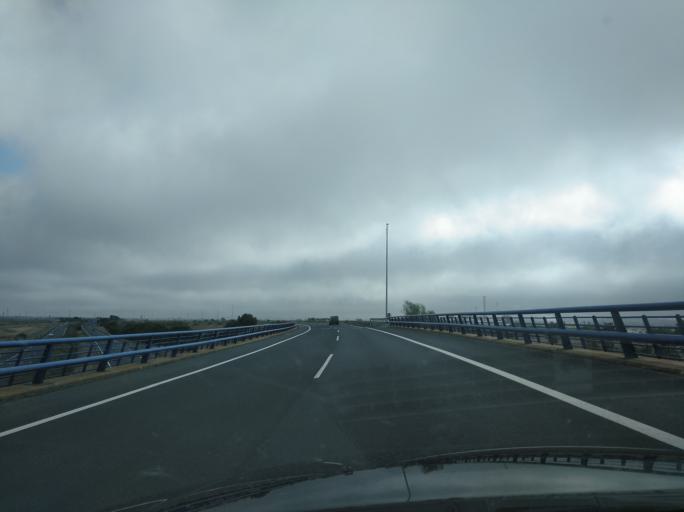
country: ES
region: Andalusia
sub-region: Provincia de Huelva
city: San Juan del Puerto
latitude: 37.3119
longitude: -6.8797
